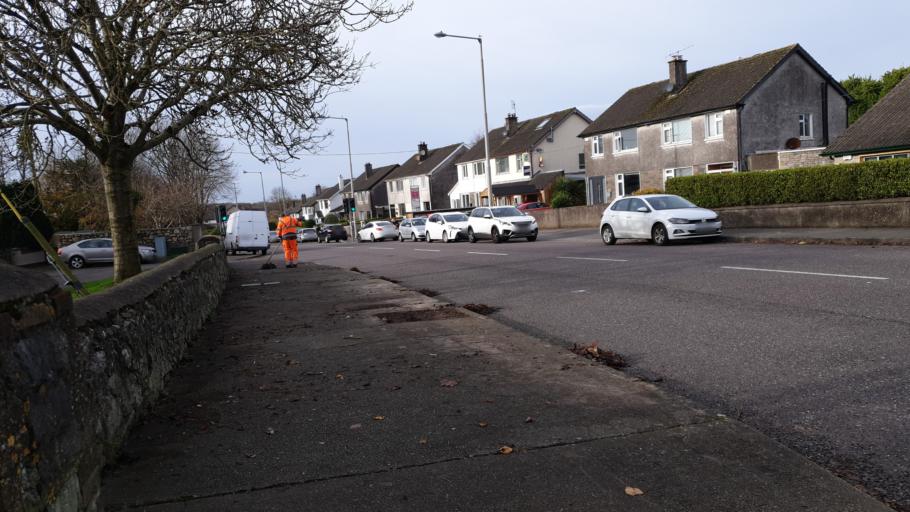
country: IE
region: Munster
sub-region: County Cork
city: Passage West
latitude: 51.8944
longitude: -8.4054
